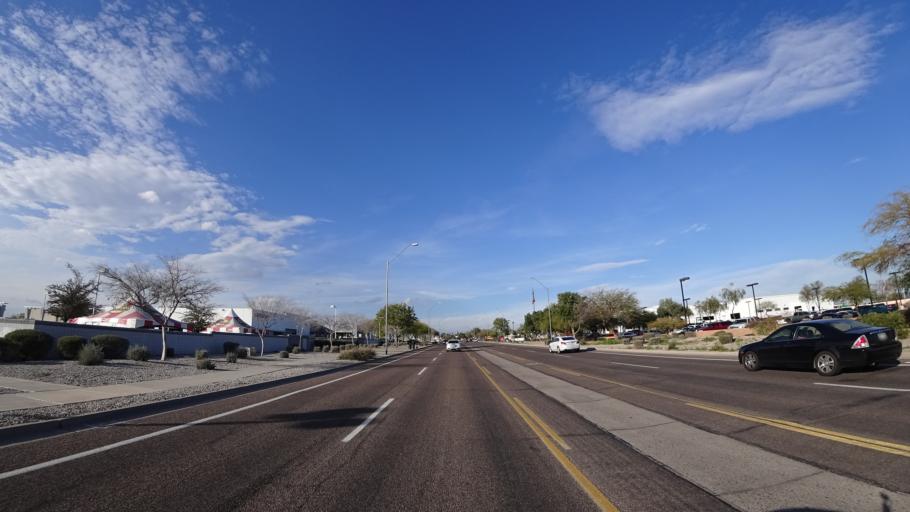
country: US
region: Arizona
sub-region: Maricopa County
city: Sun City
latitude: 33.6355
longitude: -112.2529
